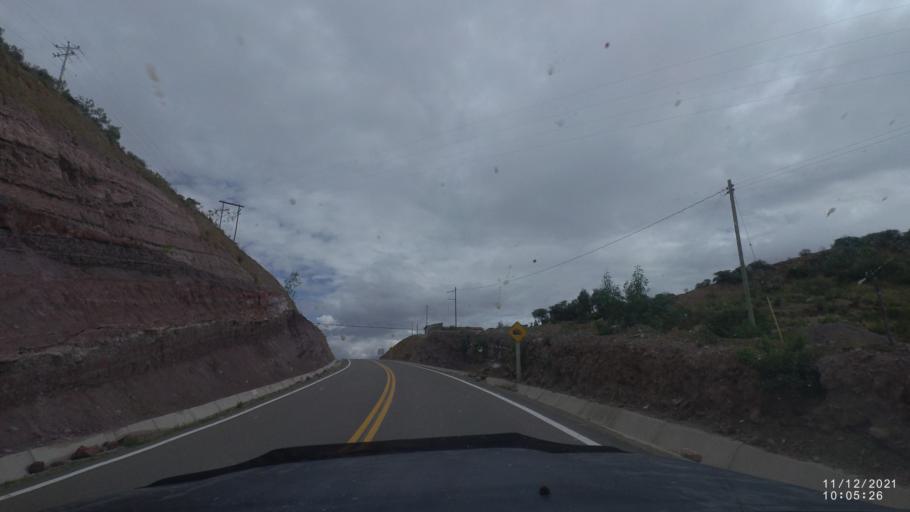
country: BO
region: Cochabamba
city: Cliza
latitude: -17.6998
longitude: -65.9474
